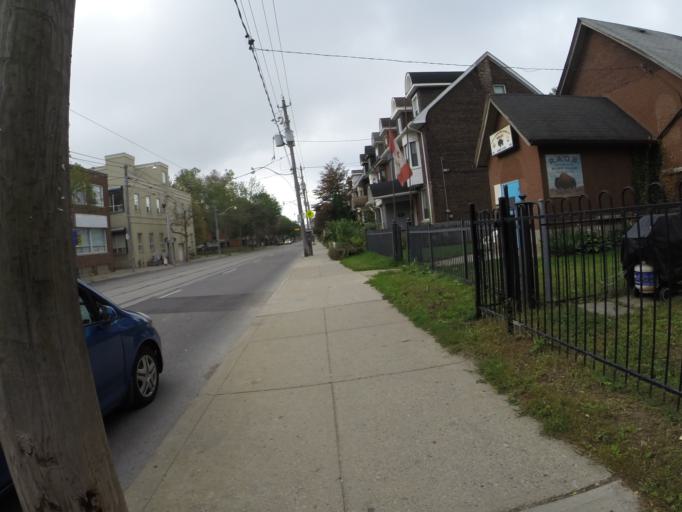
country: CA
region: Ontario
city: Toronto
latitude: 43.6632
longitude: -79.3518
